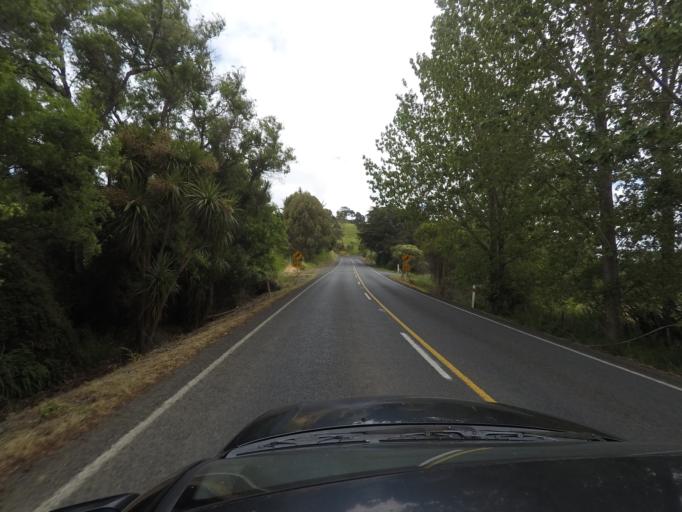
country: NZ
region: Auckland
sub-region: Auckland
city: Parakai
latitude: -36.5338
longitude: 174.4565
